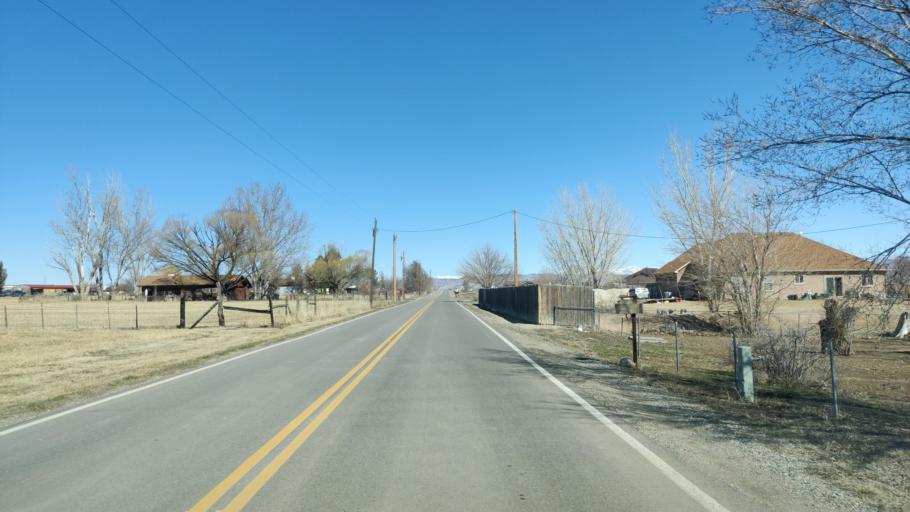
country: US
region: Colorado
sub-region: Mesa County
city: Fruita
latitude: 39.1804
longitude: -108.7105
